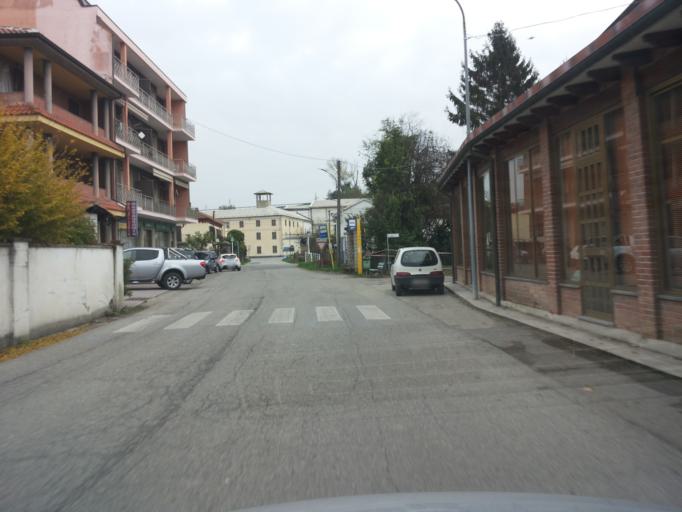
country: IT
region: Piedmont
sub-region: Provincia di Alessandria
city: Cereseto
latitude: 45.1023
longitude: 8.3078
